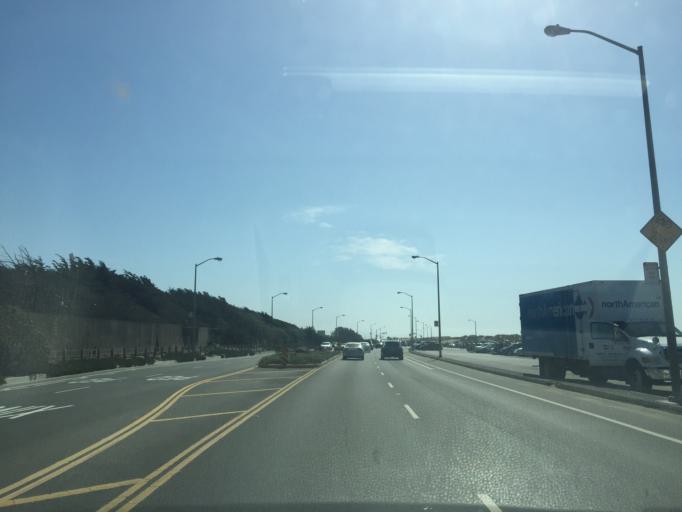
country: US
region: California
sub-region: San Mateo County
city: Daly City
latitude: 37.7674
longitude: -122.5104
